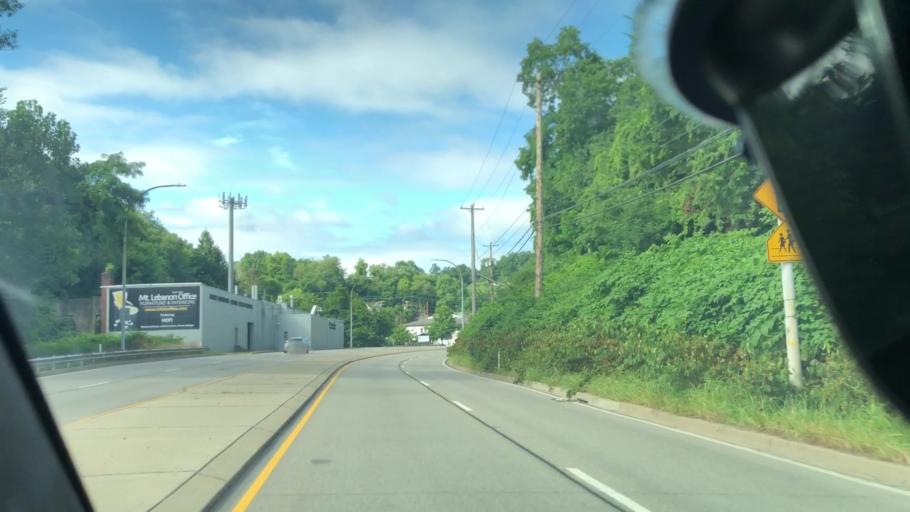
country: US
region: Pennsylvania
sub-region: Allegheny County
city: Dormont
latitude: 40.4087
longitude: -80.0324
